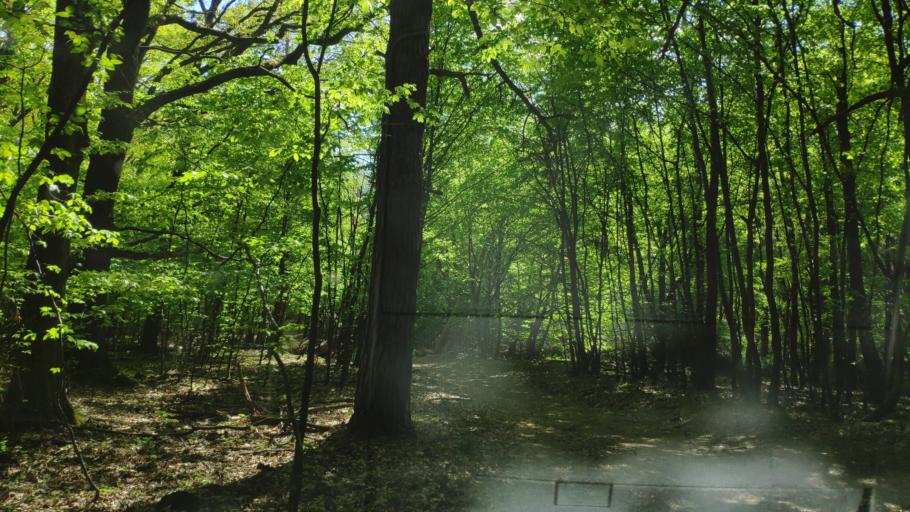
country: SK
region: Kosicky
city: Kosice
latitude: 48.6661
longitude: 21.4309
